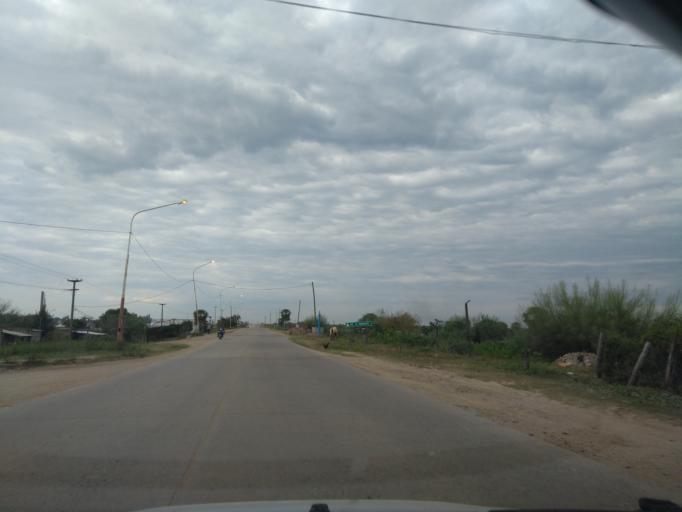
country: AR
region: Chaco
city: Puerto Vilelas
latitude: -27.5211
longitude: -58.9404
